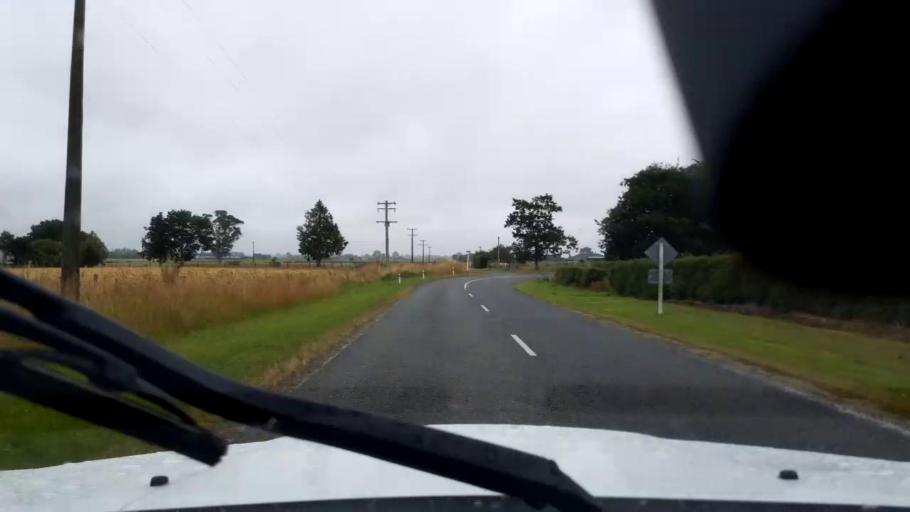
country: NZ
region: Canterbury
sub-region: Timaru District
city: Pleasant Point
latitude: -44.2524
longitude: 171.2200
